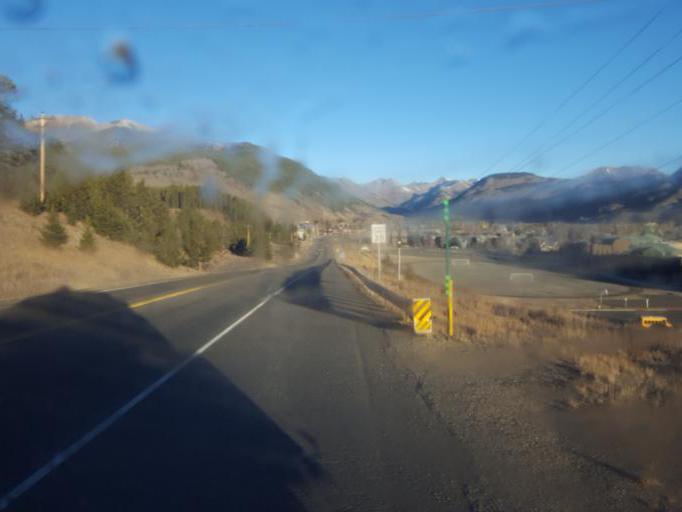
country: US
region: Colorado
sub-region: Gunnison County
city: Crested Butte
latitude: 38.8628
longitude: -106.9748
